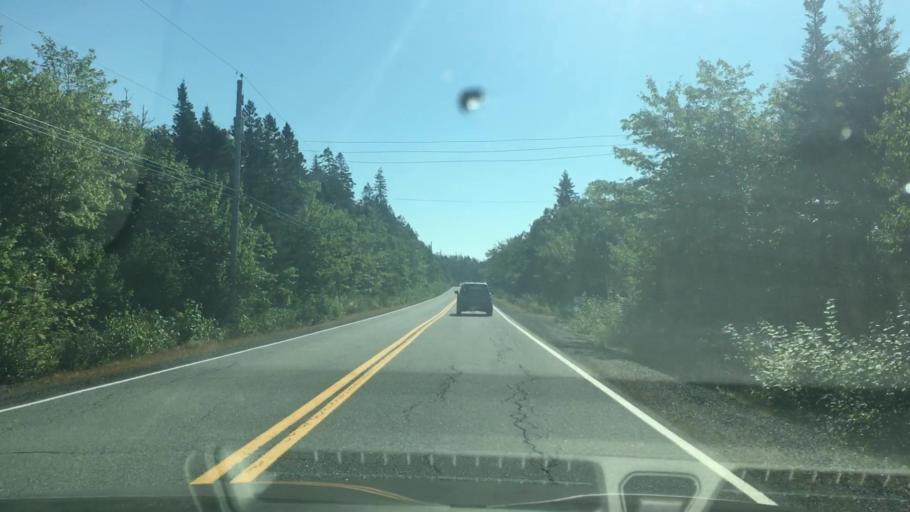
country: CA
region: Nova Scotia
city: Cole Harbour
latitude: 44.8133
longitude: -62.8417
